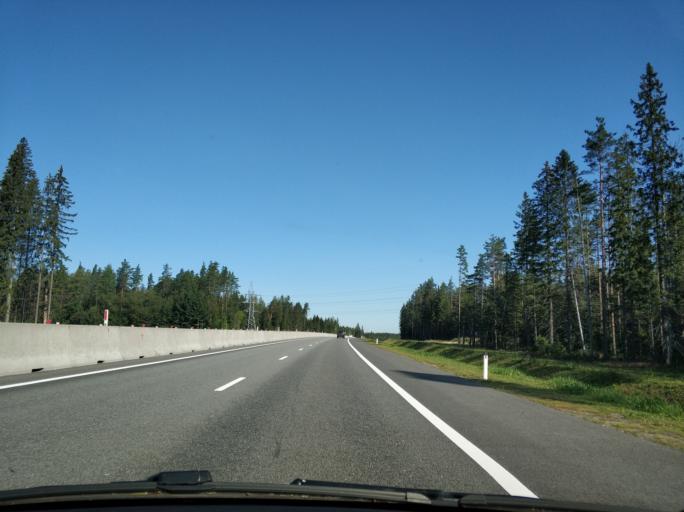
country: RU
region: Leningrad
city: Sosnovo
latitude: 60.5224
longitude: 30.1708
